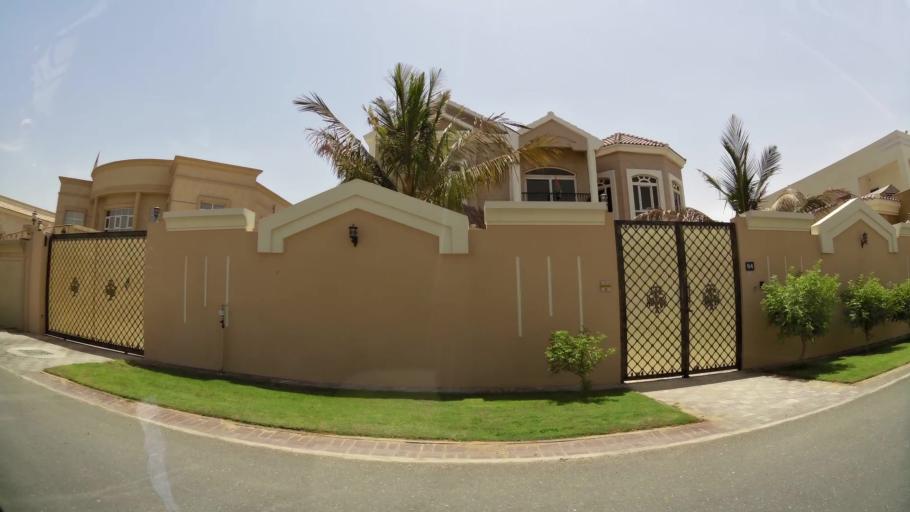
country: AE
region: Ash Shariqah
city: Sharjah
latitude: 25.1938
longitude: 55.4194
